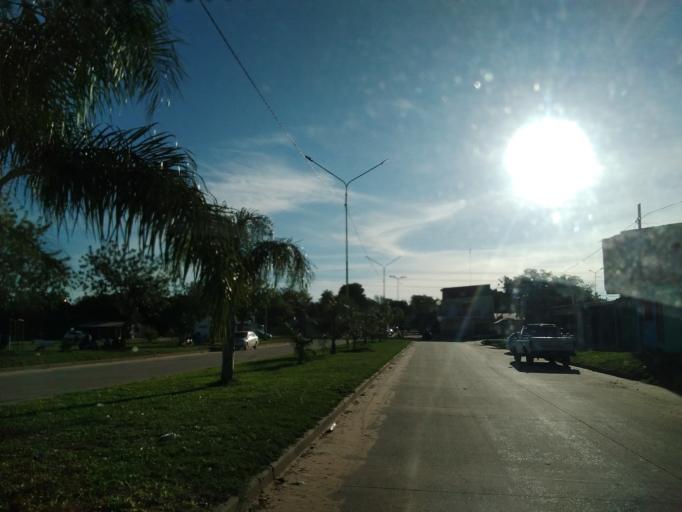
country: AR
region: Corrientes
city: Corrientes
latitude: -27.5085
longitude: -58.7971
